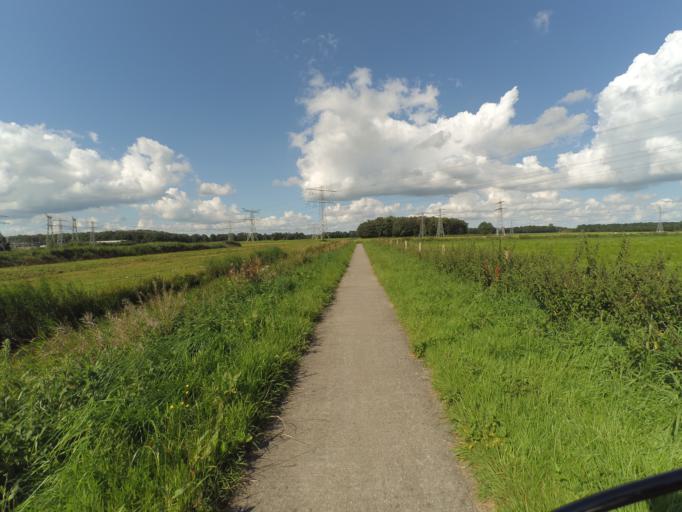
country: NL
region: Friesland
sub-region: Gemeente Tytsjerksteradiel
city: Noardburgum
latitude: 53.2160
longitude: 6.0310
